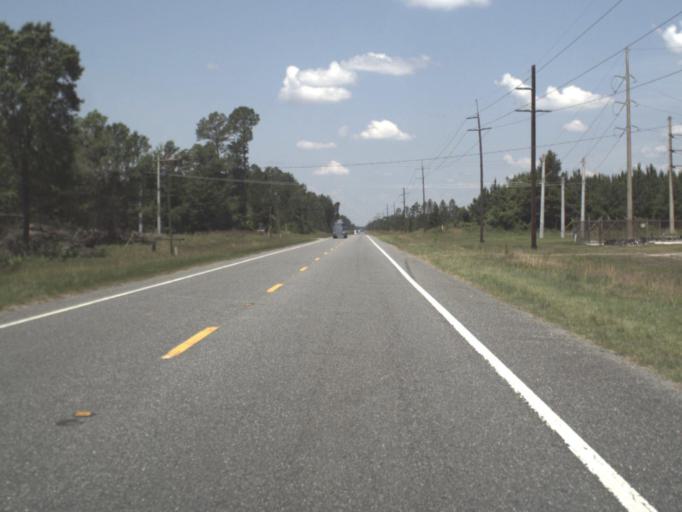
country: US
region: Florida
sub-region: Bradford County
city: Starke
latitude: 29.9694
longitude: -82.2048
